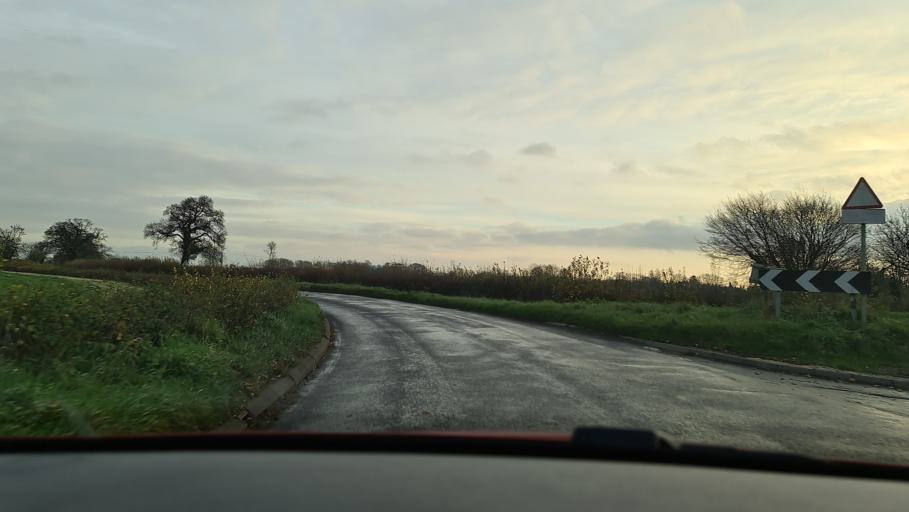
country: GB
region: England
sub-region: Oxfordshire
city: Kidlington
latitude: 51.8304
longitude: -1.2122
